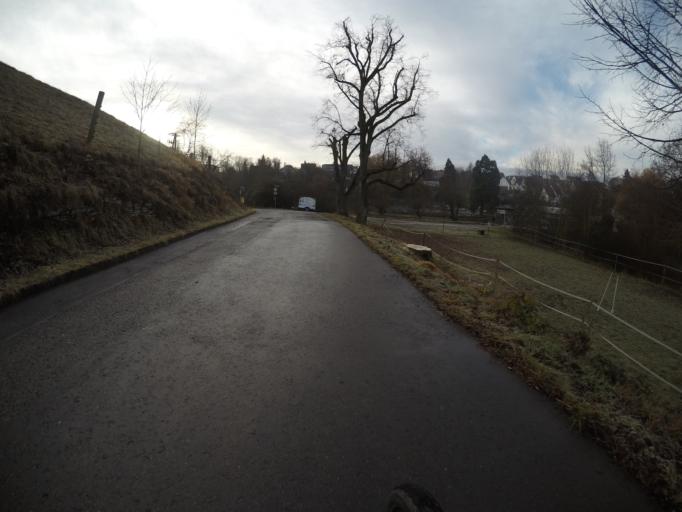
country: DE
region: Baden-Wuerttemberg
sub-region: Regierungsbezirk Stuttgart
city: Ehningen
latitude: 48.6957
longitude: 8.9429
